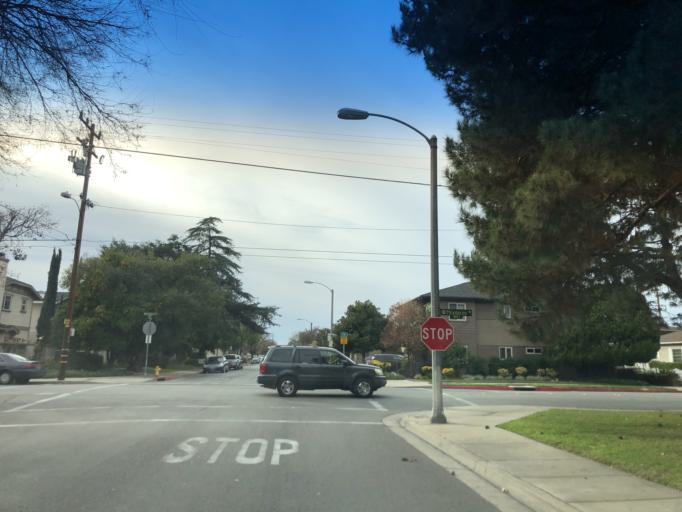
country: US
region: California
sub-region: Los Angeles County
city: Monrovia
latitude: 34.1425
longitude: -118.0140
